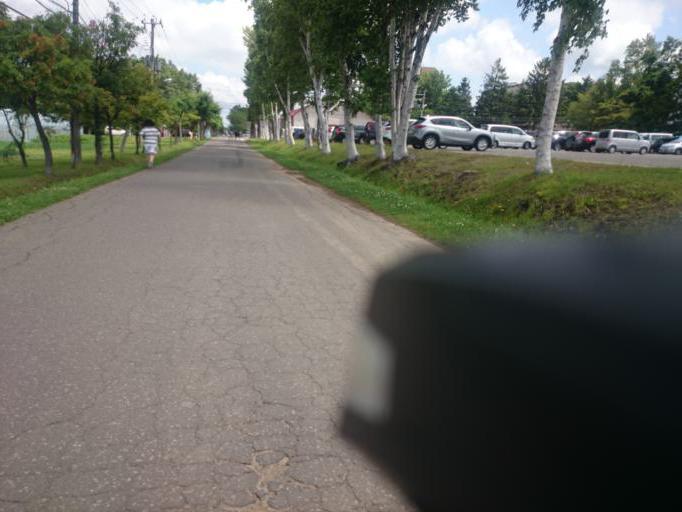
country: JP
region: Hokkaido
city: Ebetsu
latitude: 43.0718
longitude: 141.5054
